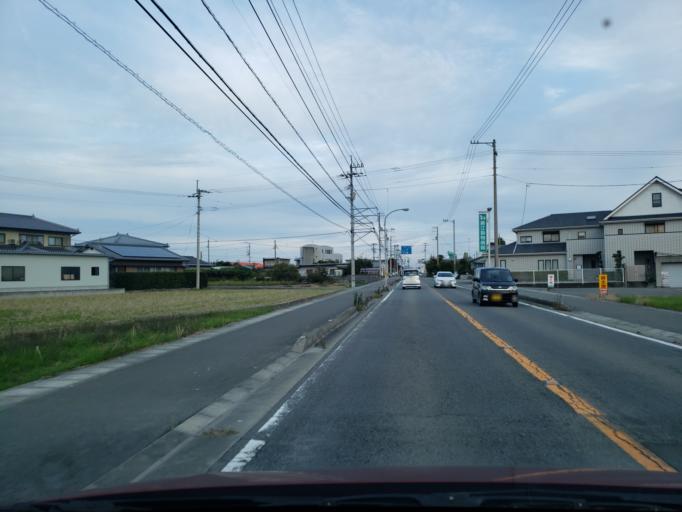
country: JP
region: Tokushima
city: Kamojimacho-jogejima
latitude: 34.1001
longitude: 134.3362
